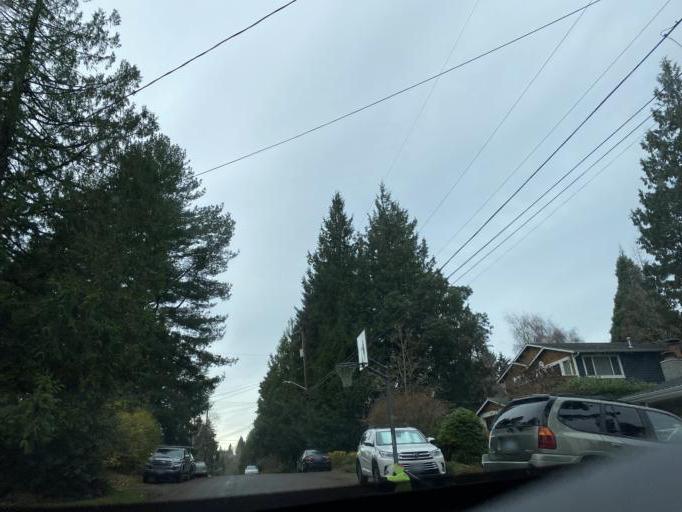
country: US
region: Washington
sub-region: King County
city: Lake Forest Park
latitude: 47.6966
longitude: -122.3001
